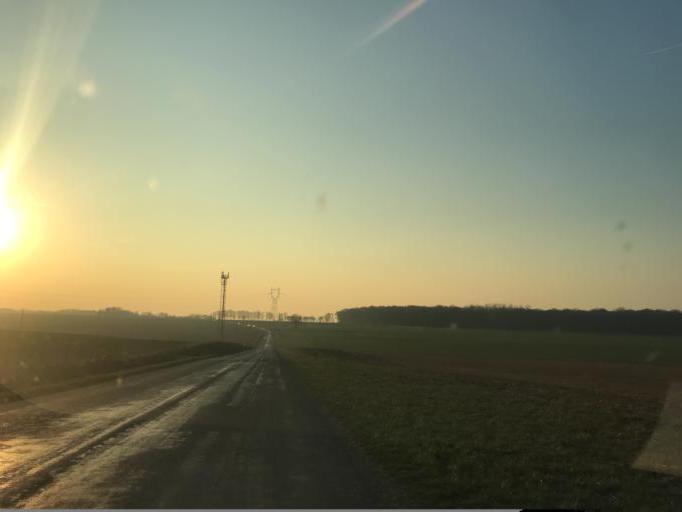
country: FR
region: Ile-de-France
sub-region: Departement de Seine-et-Marne
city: Juilly
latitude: 49.0163
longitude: 2.7321
